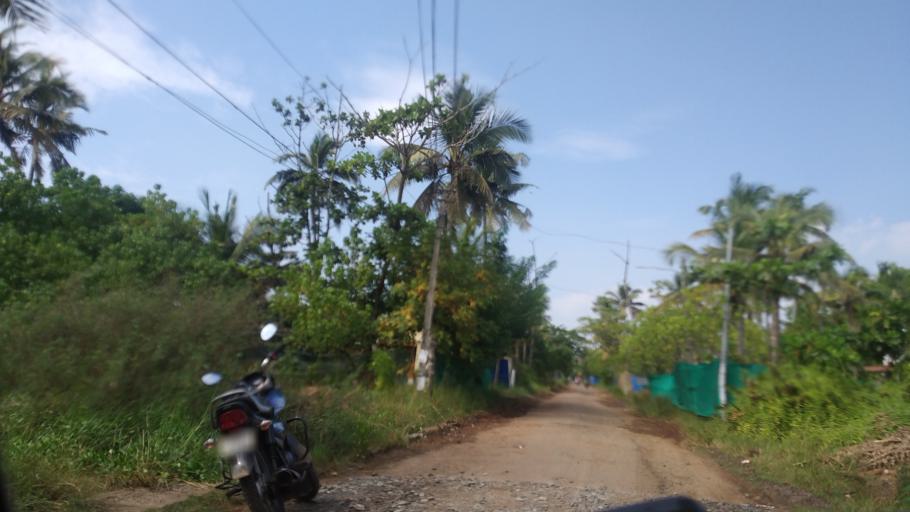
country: IN
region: Kerala
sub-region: Ernakulam
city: Elur
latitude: 10.0657
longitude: 76.1993
